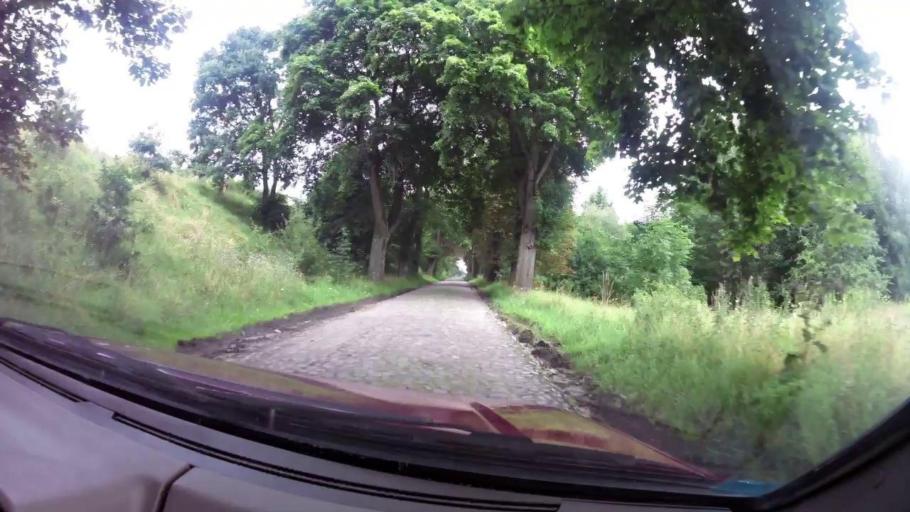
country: PL
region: West Pomeranian Voivodeship
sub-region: Powiat swidwinski
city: Polczyn-Zdroj
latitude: 53.7923
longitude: 16.0411
